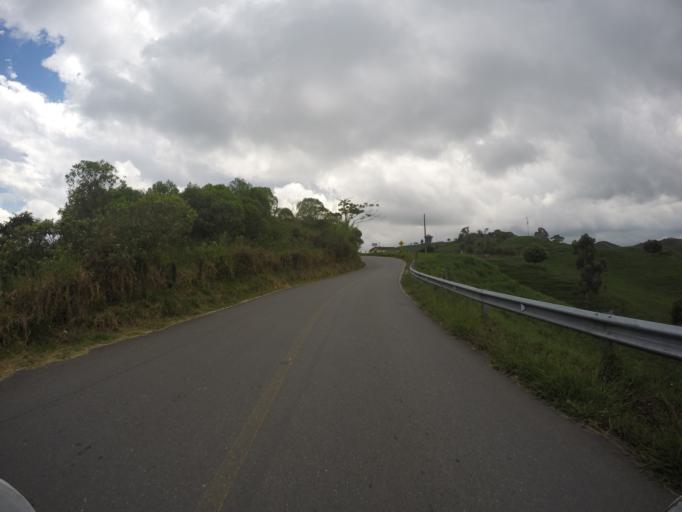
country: CO
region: Quindio
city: Filandia
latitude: 4.6638
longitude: -75.6717
